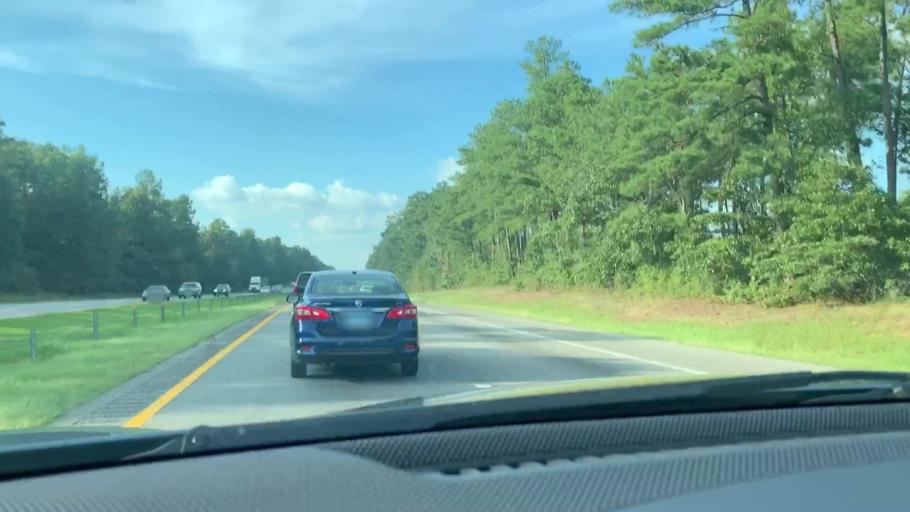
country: US
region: South Carolina
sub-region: Orangeburg County
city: Brookdale
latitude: 33.6026
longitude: -80.8604
